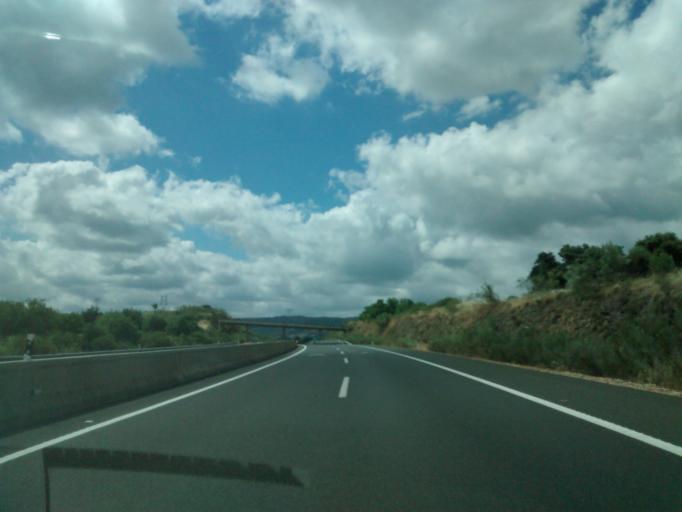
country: ES
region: Extremadura
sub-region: Provincia de Caceres
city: Casas de Miravete
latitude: 39.7458
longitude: -5.7265
